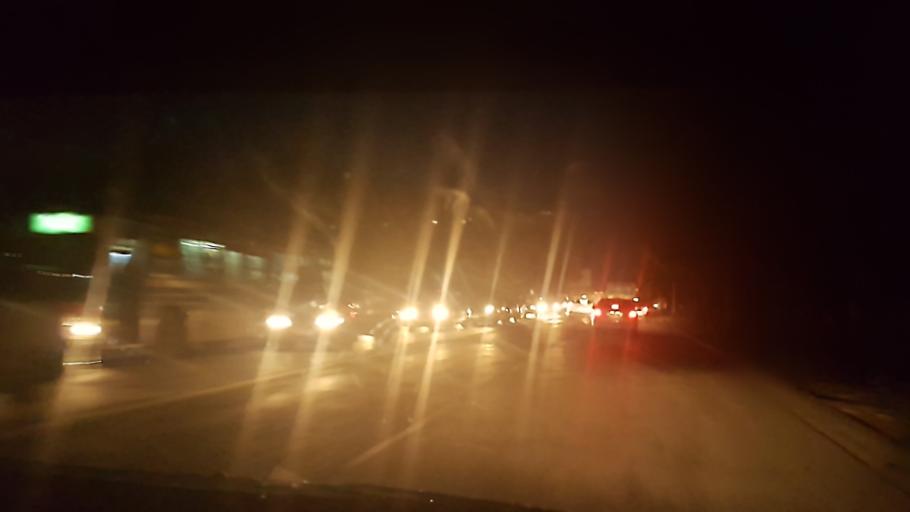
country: MM
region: Yangon
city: Yangon
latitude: 16.7822
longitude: 96.1675
